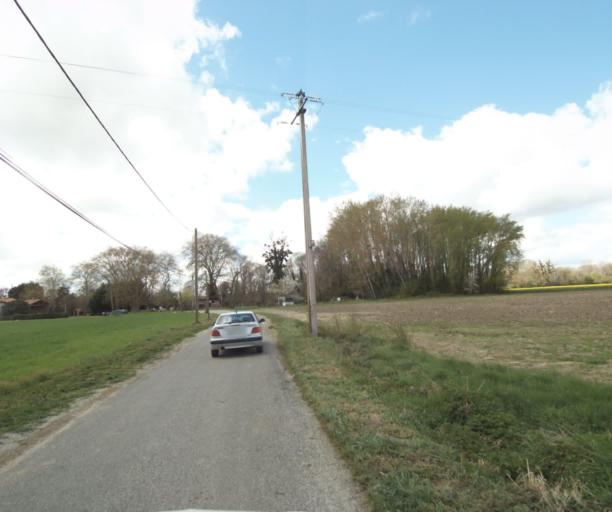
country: FR
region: Midi-Pyrenees
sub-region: Departement de l'Ariege
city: Saverdun
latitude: 43.2613
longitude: 1.5821
